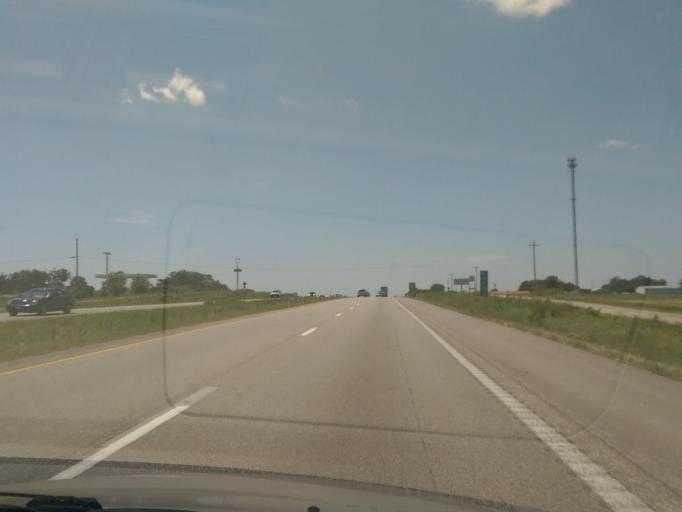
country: US
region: Missouri
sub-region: Saline County
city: Sweet Springs
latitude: 38.9714
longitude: -93.2645
